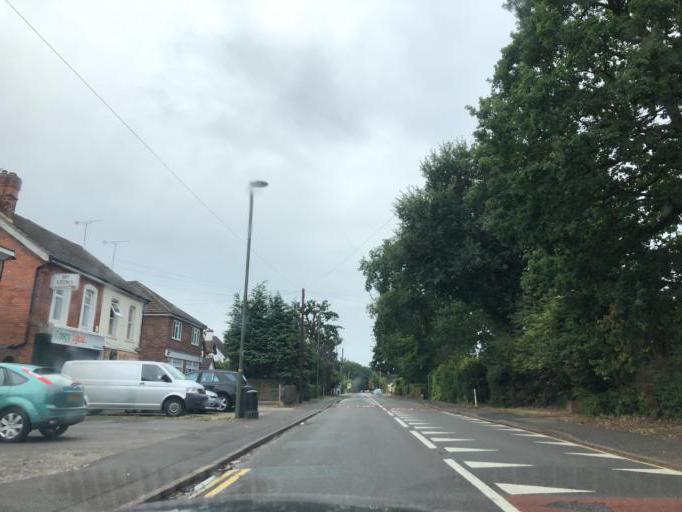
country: GB
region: England
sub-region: Hampshire
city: Farnborough
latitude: 51.2919
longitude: -0.7262
